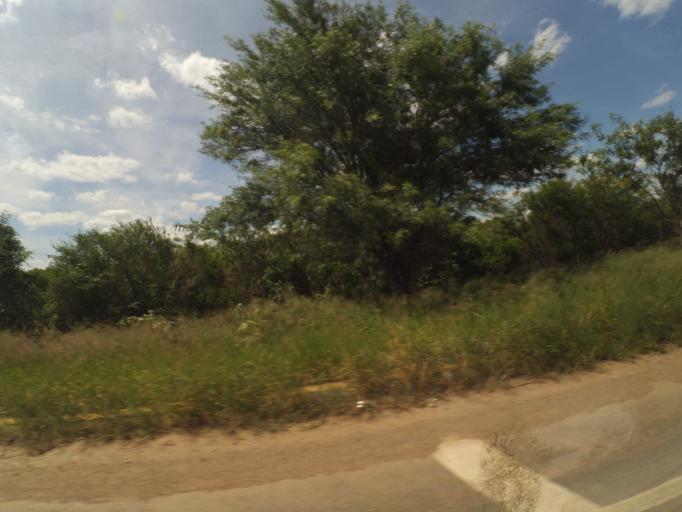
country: BO
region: Santa Cruz
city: Pailon
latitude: -17.5918
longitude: -61.9871
